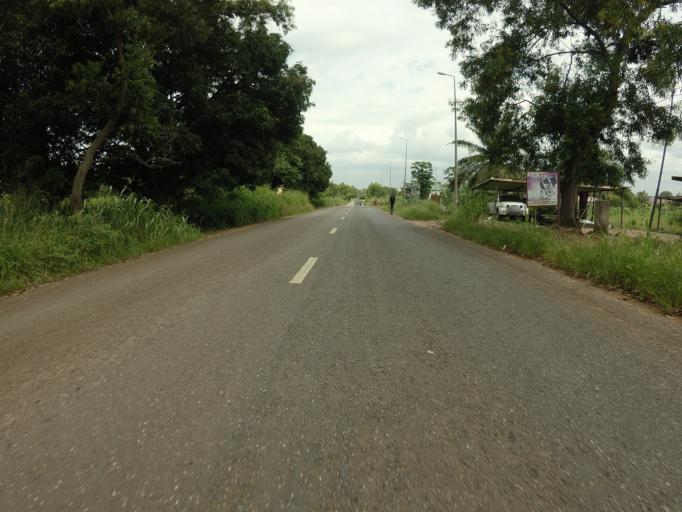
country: GH
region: Volta
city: Ho
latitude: 6.5888
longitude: 0.4628
